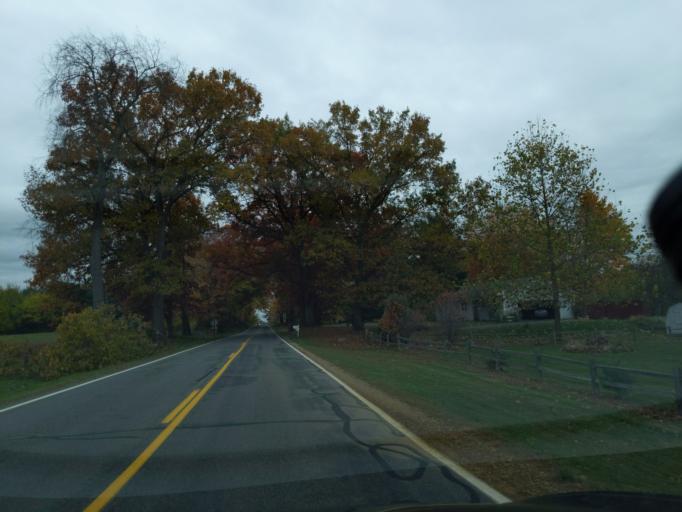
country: US
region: Michigan
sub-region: Jackson County
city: Spring Arbor
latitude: 42.2826
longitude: -84.6000
